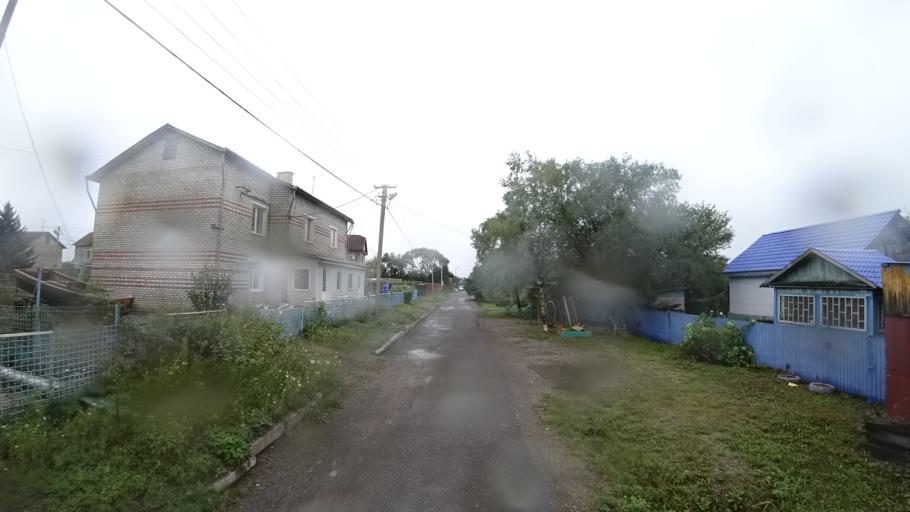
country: RU
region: Primorskiy
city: Monastyrishche
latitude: 44.2013
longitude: 132.4282
